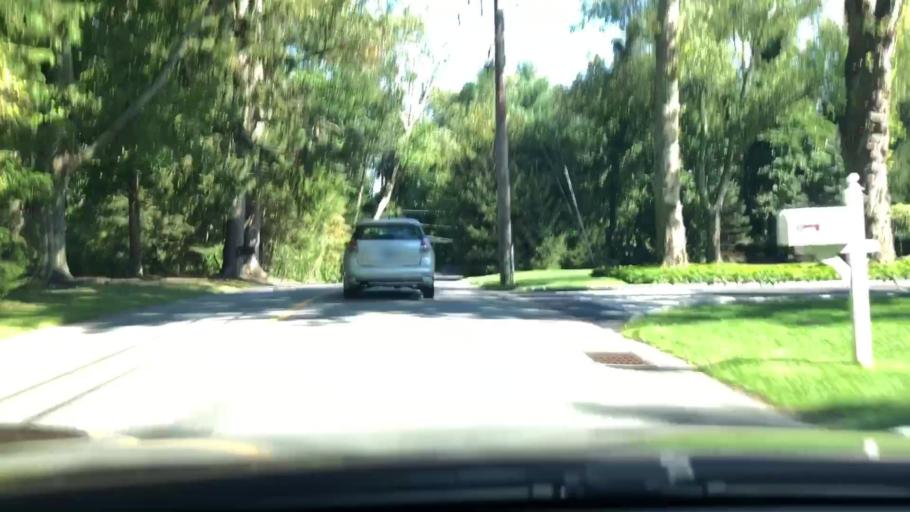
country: US
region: Connecticut
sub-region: Fairfield County
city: Darien
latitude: 41.1121
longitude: -73.4806
